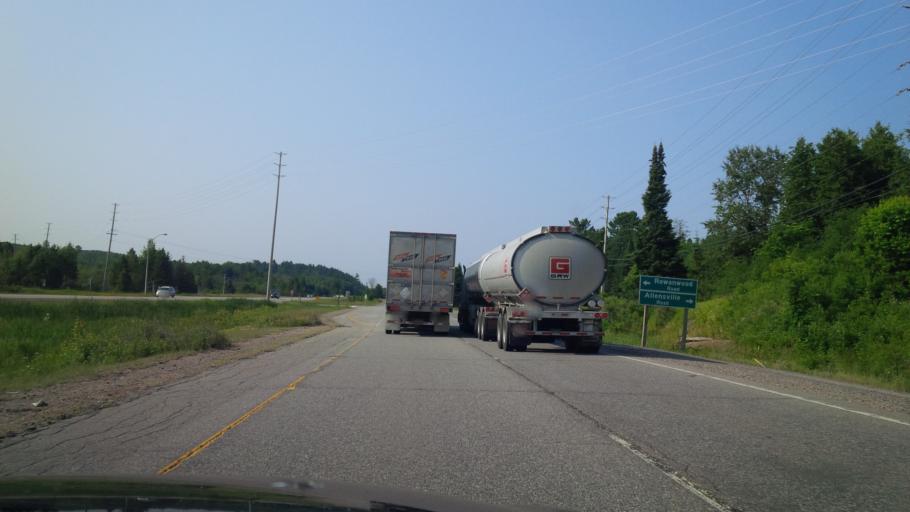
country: CA
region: Ontario
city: Huntsville
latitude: 45.2571
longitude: -79.2965
